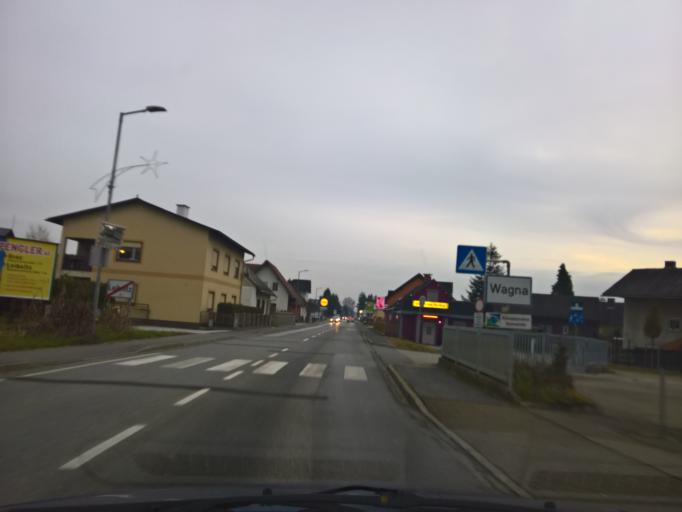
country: AT
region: Styria
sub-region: Politischer Bezirk Leibnitz
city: Leibnitz
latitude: 46.7735
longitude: 15.5525
